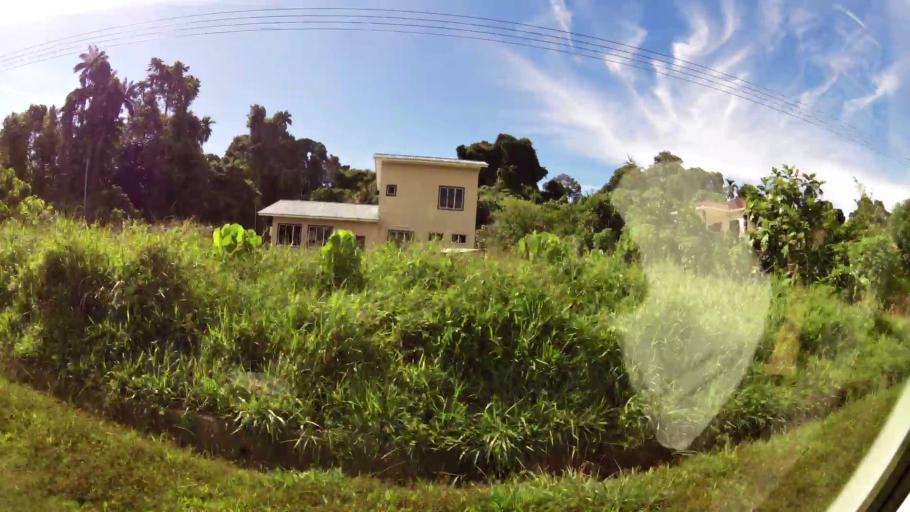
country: BN
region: Brunei and Muara
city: Bandar Seri Begawan
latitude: 5.0263
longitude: 115.0465
